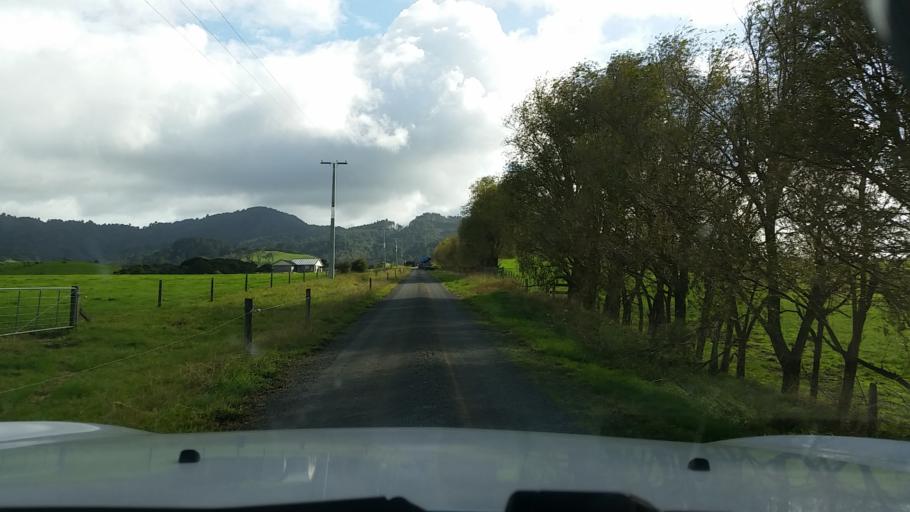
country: NZ
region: Waikato
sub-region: Hauraki District
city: Ngatea
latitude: -37.5016
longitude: 175.4051
